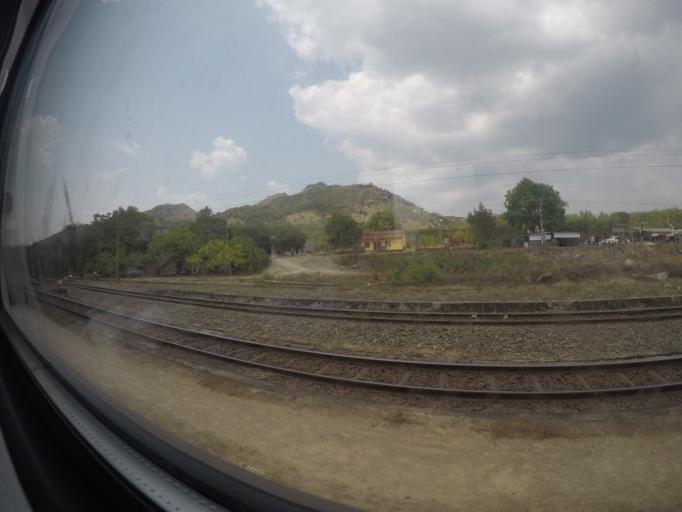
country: VN
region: Binh Thuan
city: Tanh Linh
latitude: 10.9694
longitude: 107.6292
